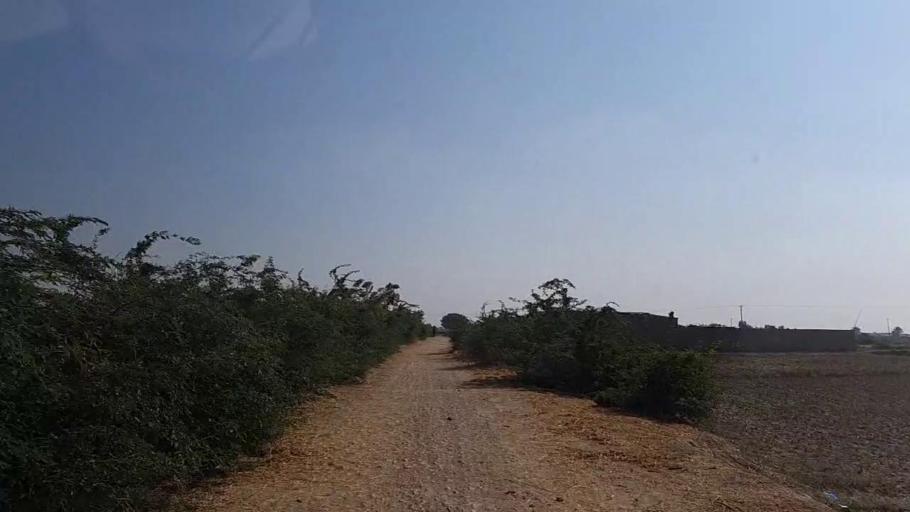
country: PK
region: Sindh
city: Thatta
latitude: 24.7669
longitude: 67.9424
